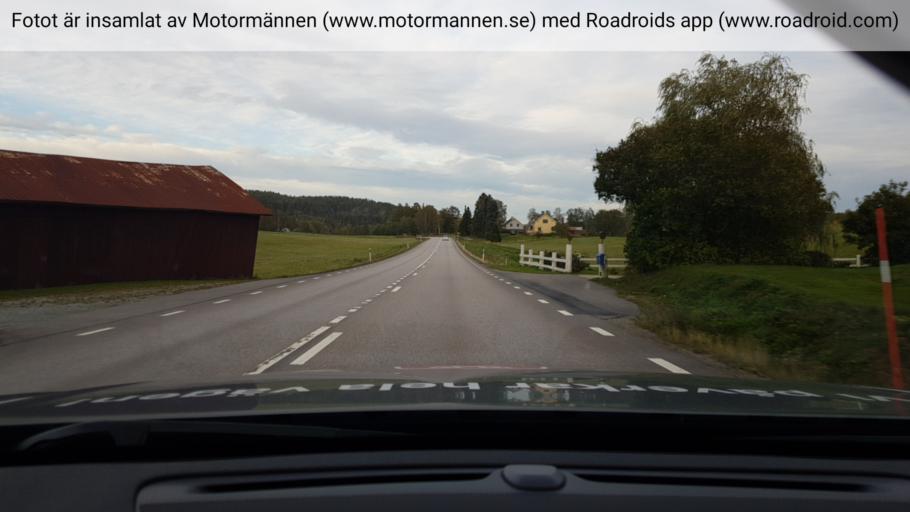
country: SE
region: Vaestra Goetaland
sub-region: Bengtsfors Kommun
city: Billingsfors
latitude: 59.0297
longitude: 12.3039
